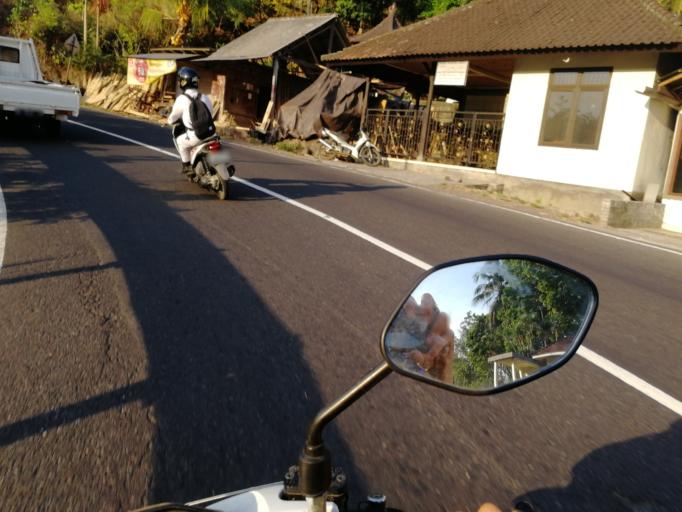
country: ID
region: Bali
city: Tistagede
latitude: -8.3737
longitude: 115.6091
